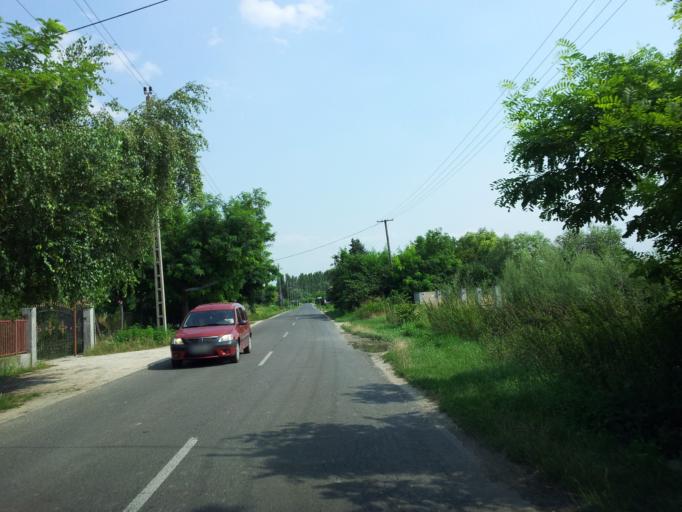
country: HU
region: Pest
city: Rackeve
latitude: 47.1849
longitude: 18.9371
